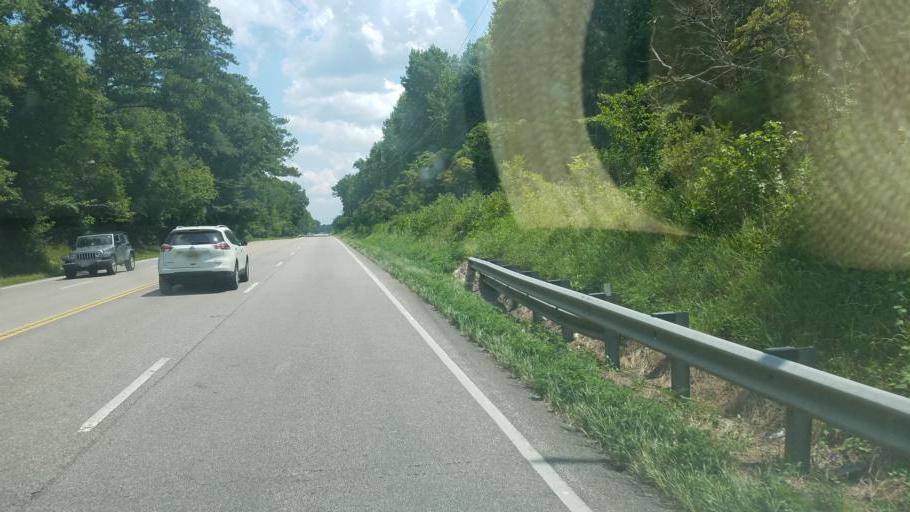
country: US
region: Virginia
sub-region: Isle of Wight County
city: Windsor
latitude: 36.8781
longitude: -76.8498
